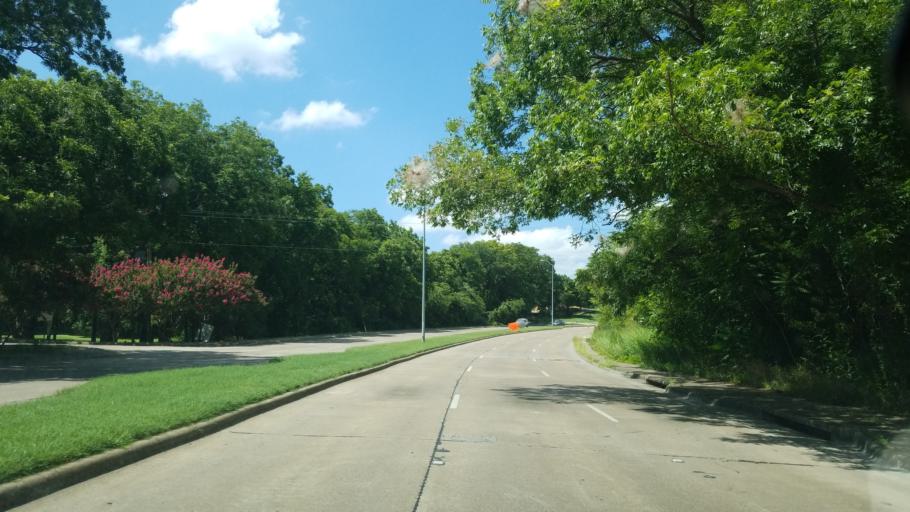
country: US
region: Texas
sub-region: Dallas County
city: Balch Springs
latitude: 32.7593
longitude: -96.7017
